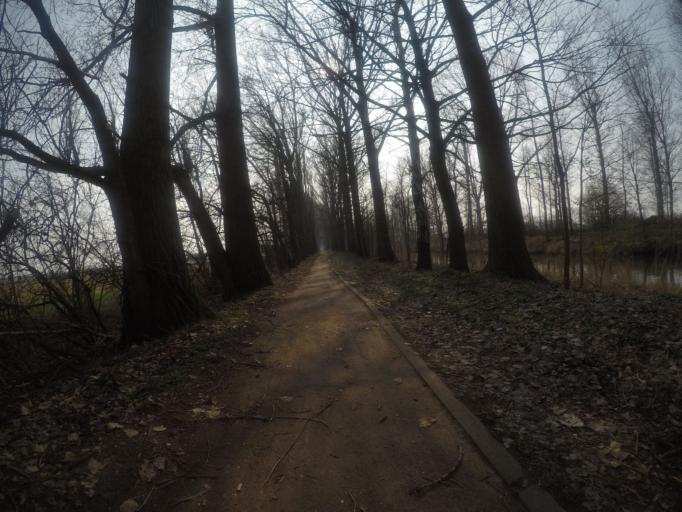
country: DE
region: Brandenburg
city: Mittenwalde
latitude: 52.2728
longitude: 13.5613
